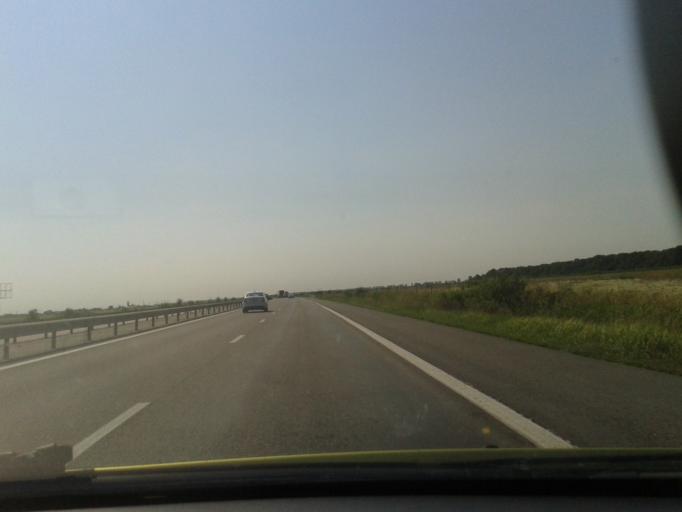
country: RO
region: Dambovita
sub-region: Comuna Corbii Mari
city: Grozavesti
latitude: 44.5751
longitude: 25.4759
